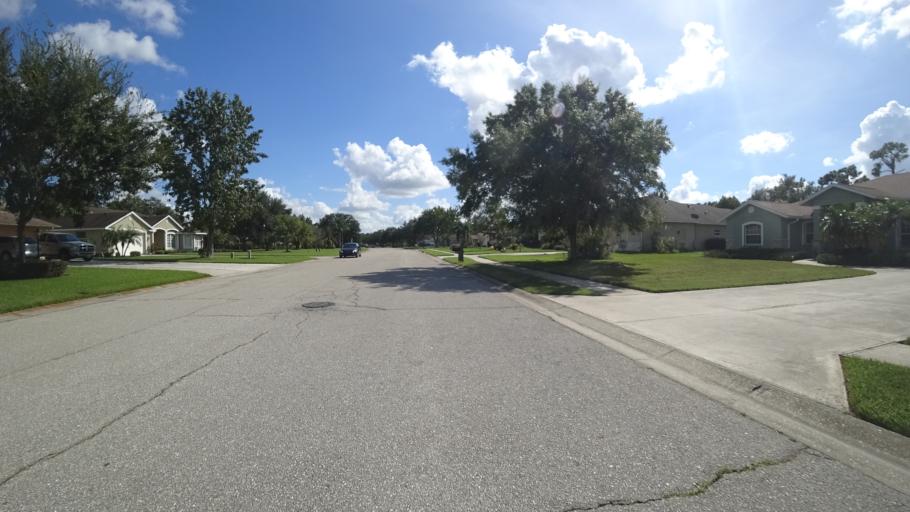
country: US
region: Florida
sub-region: Manatee County
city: Ellenton
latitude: 27.4956
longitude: -82.3964
